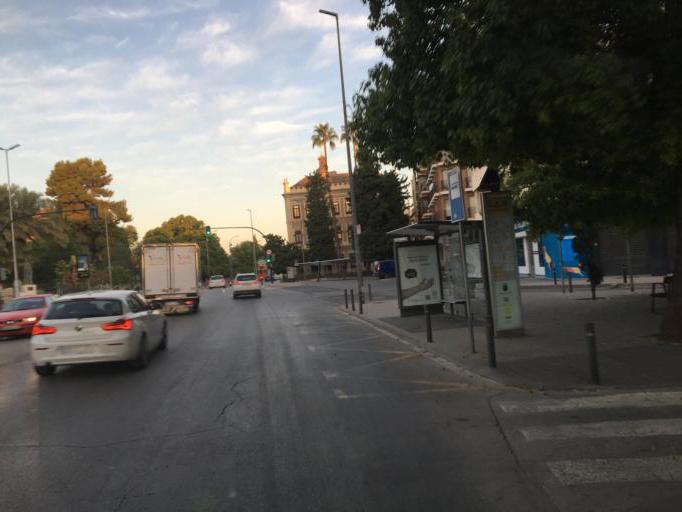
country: ES
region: Murcia
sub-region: Murcia
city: Murcia
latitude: 37.9821
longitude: -1.1258
